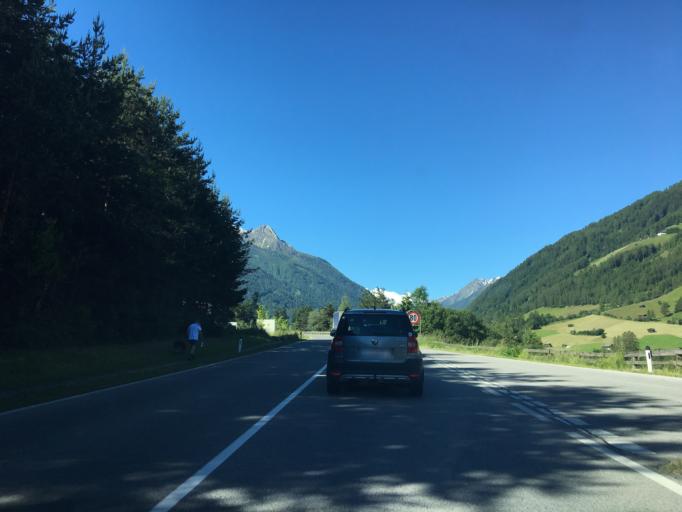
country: AT
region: Tyrol
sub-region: Politischer Bezirk Innsbruck Land
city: Fulpmes
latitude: 47.1385
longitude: 11.3420
